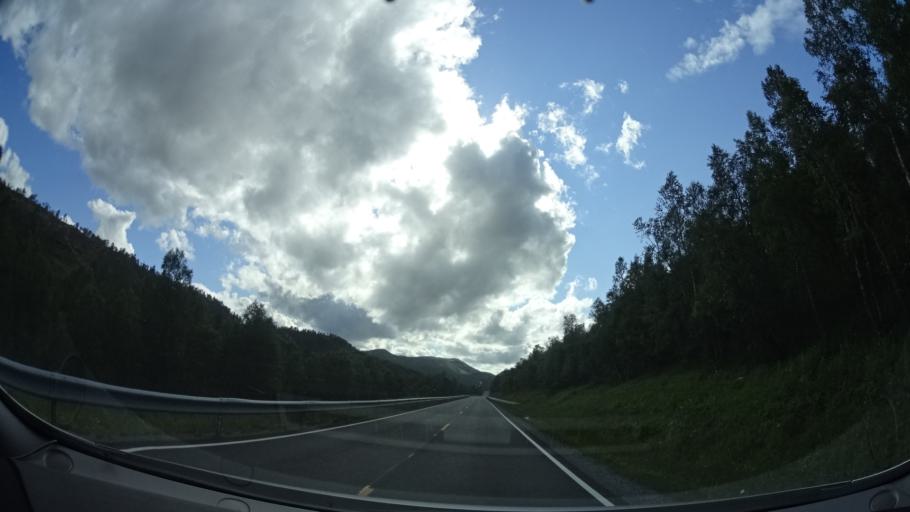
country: NO
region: More og Romsdal
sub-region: Rindal
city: Rindal
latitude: 63.2260
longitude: 9.3050
